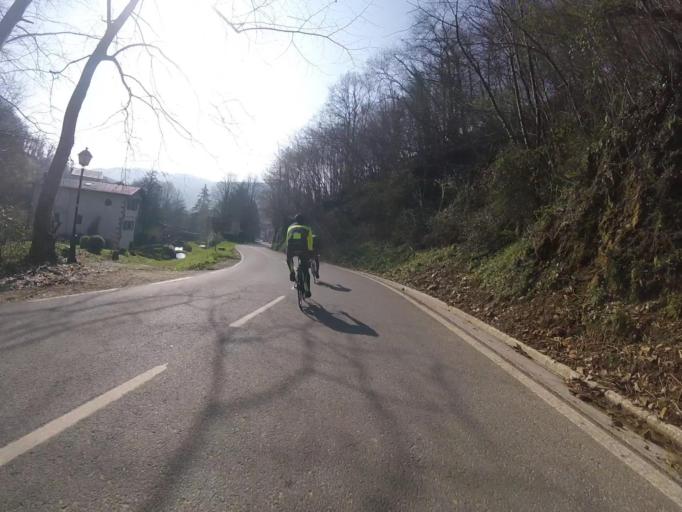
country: ES
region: Navarre
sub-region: Provincia de Navarra
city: Bera
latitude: 43.2846
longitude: -1.6796
